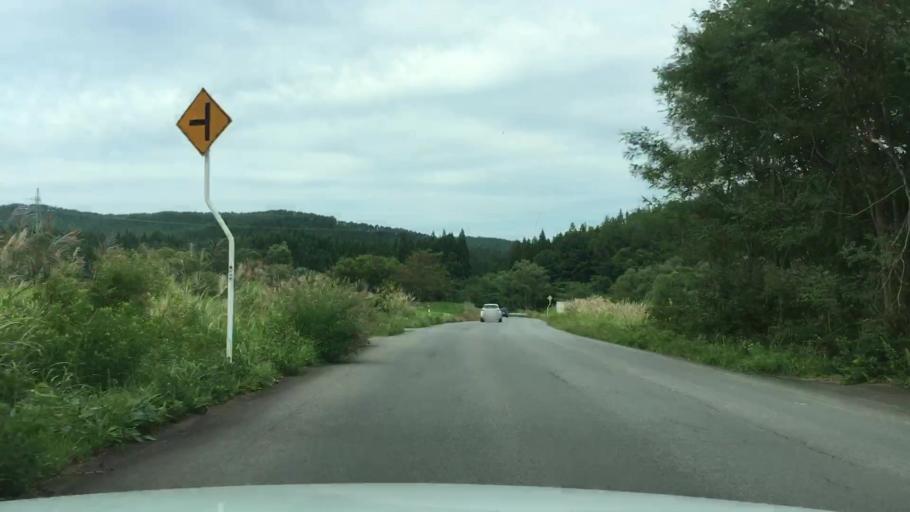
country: JP
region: Aomori
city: Shimokizukuri
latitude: 40.7131
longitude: 140.2650
